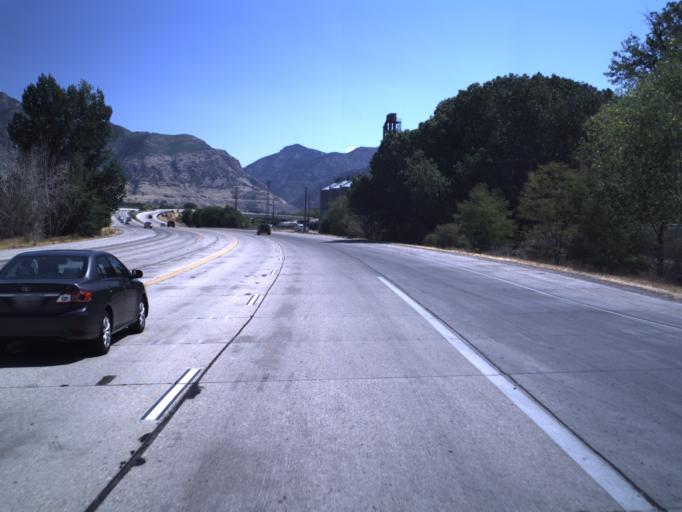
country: US
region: Utah
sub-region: Weber County
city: Ogden
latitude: 41.2299
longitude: -111.9957
